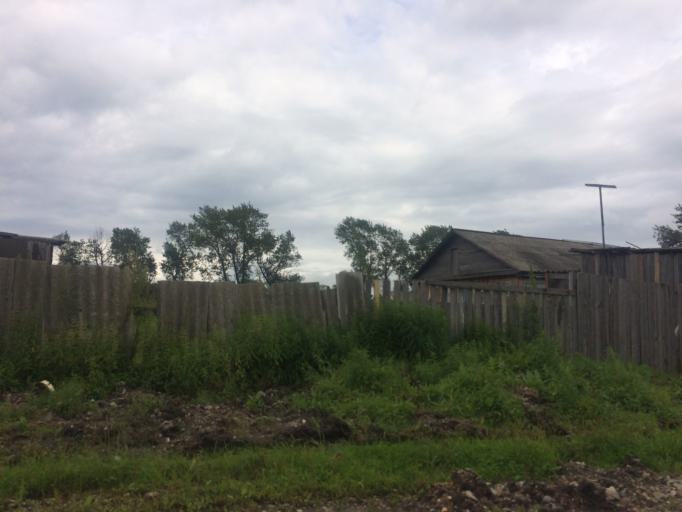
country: RU
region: Primorskiy
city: Lazo
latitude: 45.8324
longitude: 133.6123
